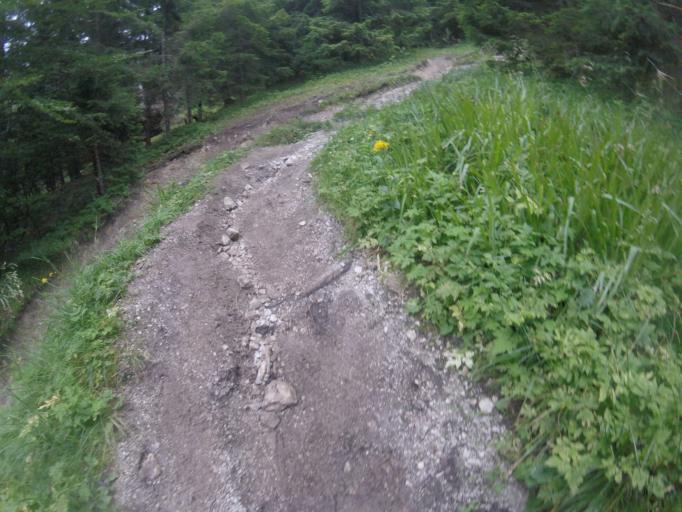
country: SK
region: Zilinsky
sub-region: Okres Zilina
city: Terchova
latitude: 49.2404
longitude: 19.1062
